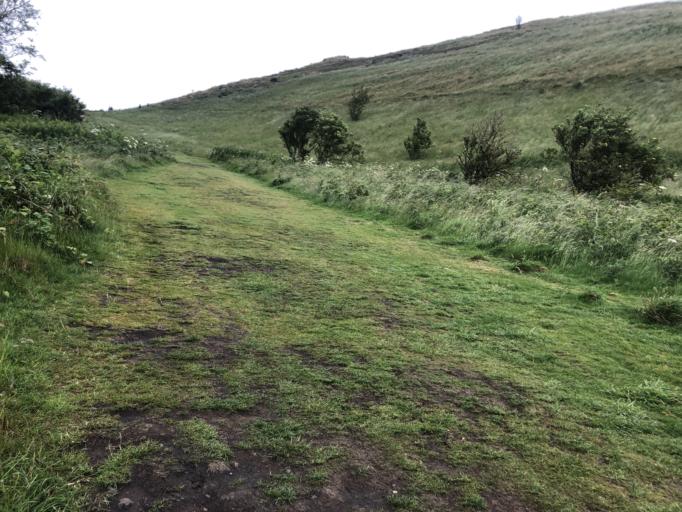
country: GB
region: Scotland
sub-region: West Lothian
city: Seafield
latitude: 55.9444
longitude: -3.1661
